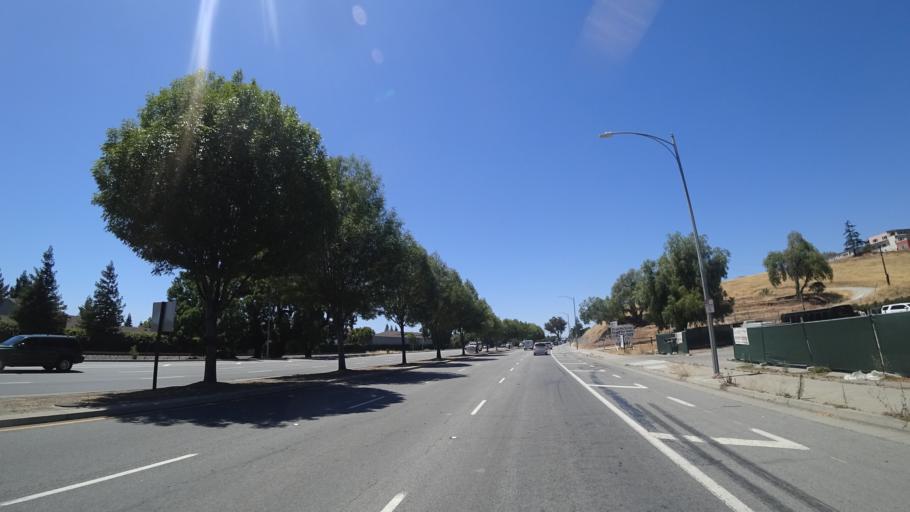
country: US
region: California
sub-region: Santa Clara County
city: Seven Trees
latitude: 37.2738
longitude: -121.8307
